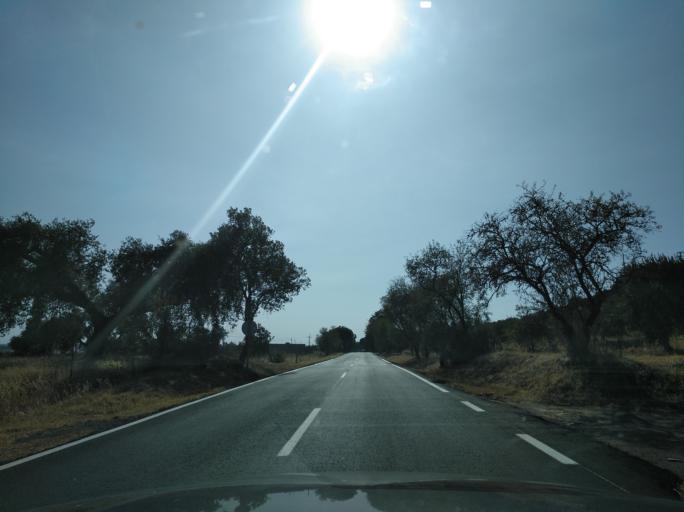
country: ES
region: Andalusia
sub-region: Provincia de Huelva
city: Rosal de la Frontera
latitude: 37.9525
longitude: -7.2879
